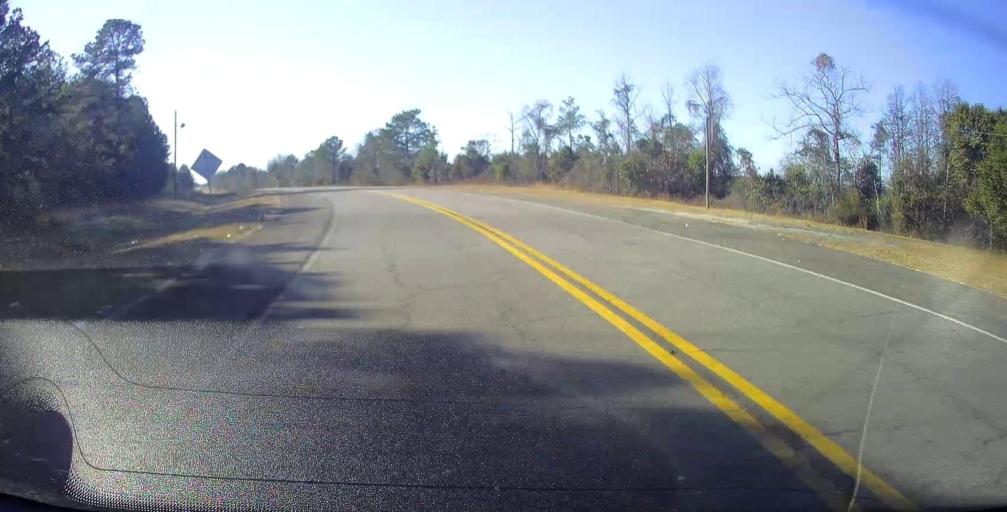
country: US
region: Georgia
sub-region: Taylor County
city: Butler
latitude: 32.5551
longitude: -84.2064
